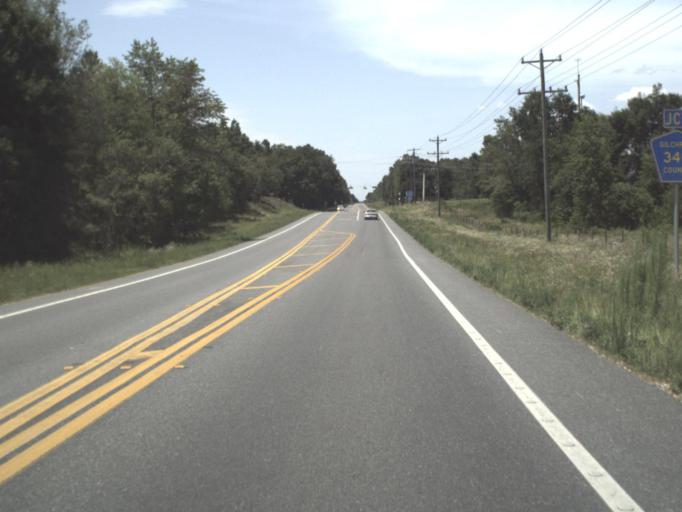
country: US
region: Florida
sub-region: Gilchrist County
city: Trenton
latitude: 29.7938
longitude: -82.8668
